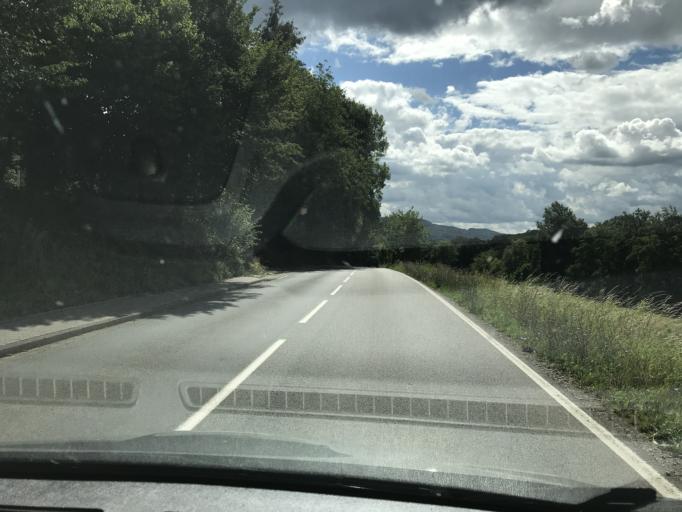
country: DE
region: Hesse
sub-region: Regierungsbezirk Darmstadt
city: Furth
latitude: 49.6626
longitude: 8.7456
